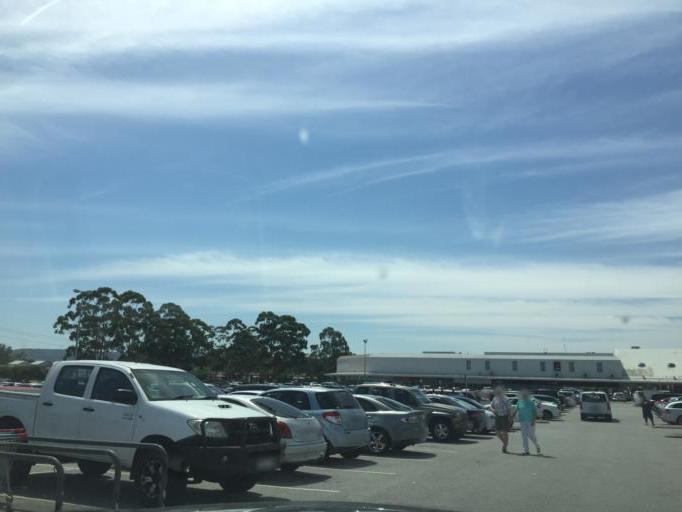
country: AU
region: Western Australia
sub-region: Gosnells
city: Maddington
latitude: -32.0520
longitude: 115.9768
